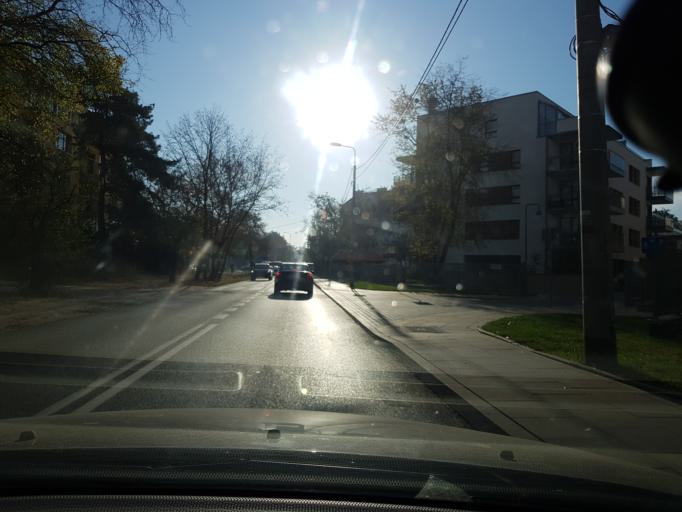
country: PL
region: Masovian Voivodeship
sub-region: Warszawa
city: Bemowo
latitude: 52.2602
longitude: 20.8956
